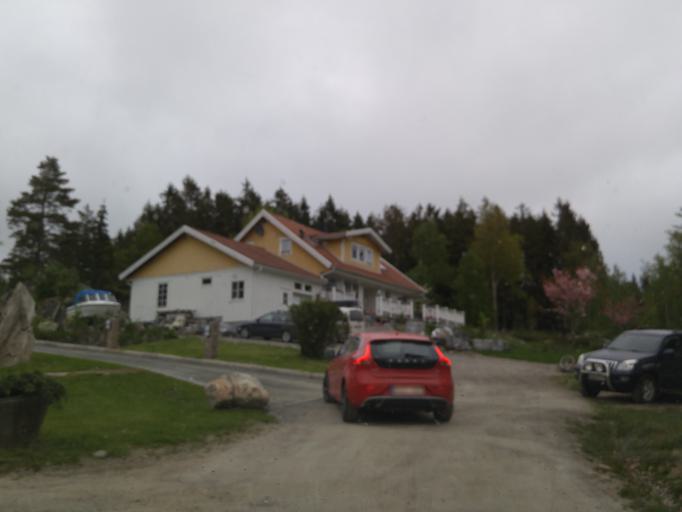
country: SE
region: Vaestra Goetaland
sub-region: Stenungsunds Kommun
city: Stora Hoga
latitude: 58.0043
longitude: 11.8685
